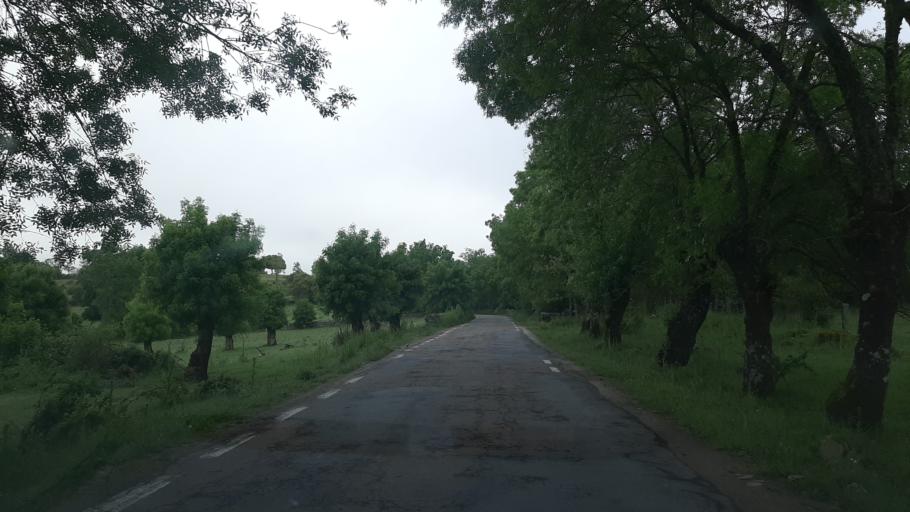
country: ES
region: Castille and Leon
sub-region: Provincia de Salamanca
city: Endrinal
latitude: 40.5508
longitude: -5.8028
